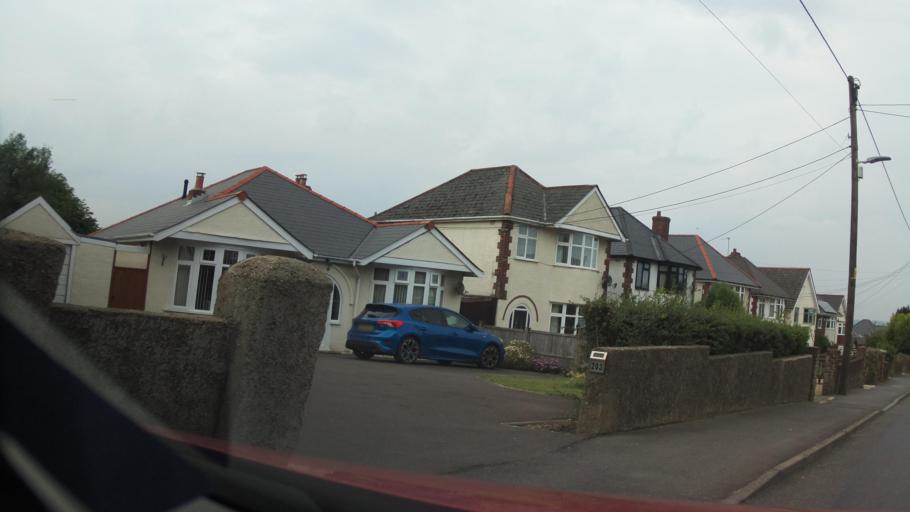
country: GB
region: England
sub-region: Somerset
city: Yeovil
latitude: 50.9574
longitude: -2.6315
